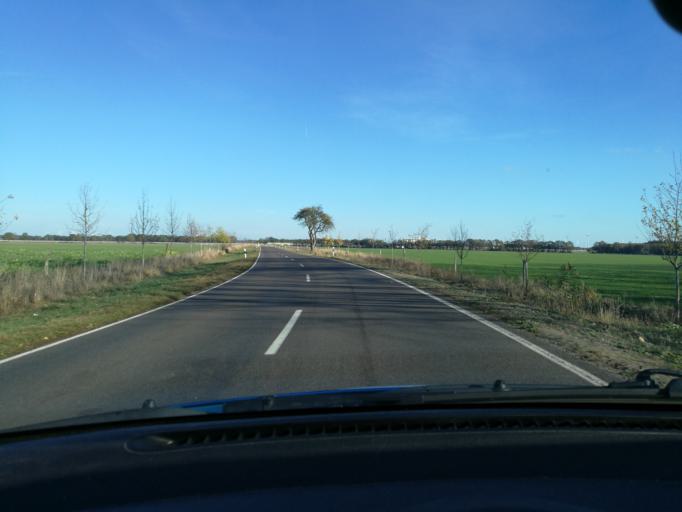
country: DE
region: Brandenburg
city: Karstadt
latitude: 53.1656
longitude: 11.6963
